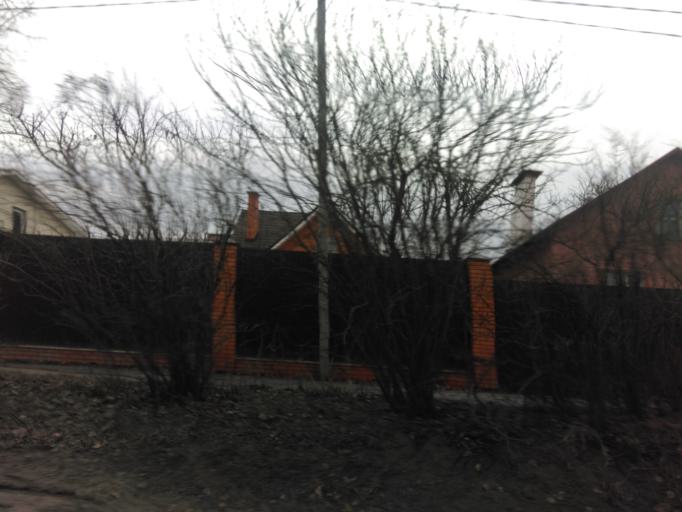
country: RU
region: Moskovskaya
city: Nikolina Gora
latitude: 55.7154
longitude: 37.0983
